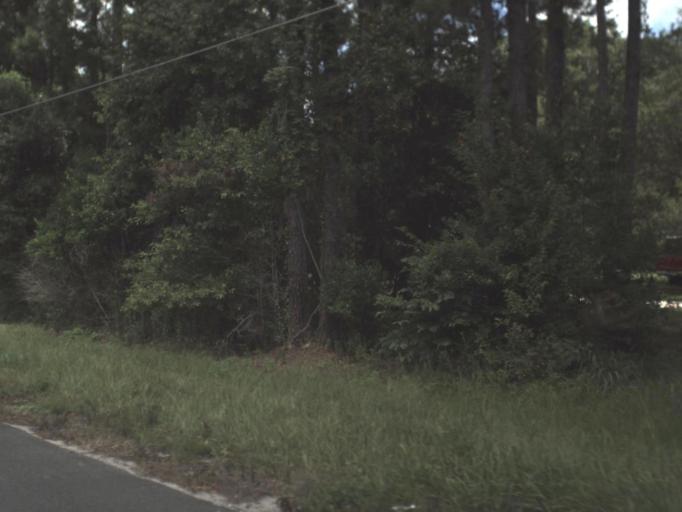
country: US
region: Florida
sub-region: Taylor County
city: Perry
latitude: 30.1058
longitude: -83.6055
